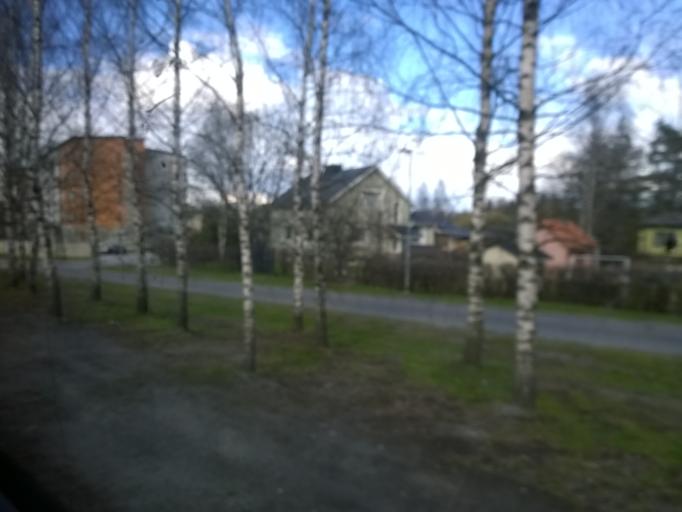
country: FI
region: Pirkanmaa
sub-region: Tampere
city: Tampere
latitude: 61.4731
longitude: 23.7749
